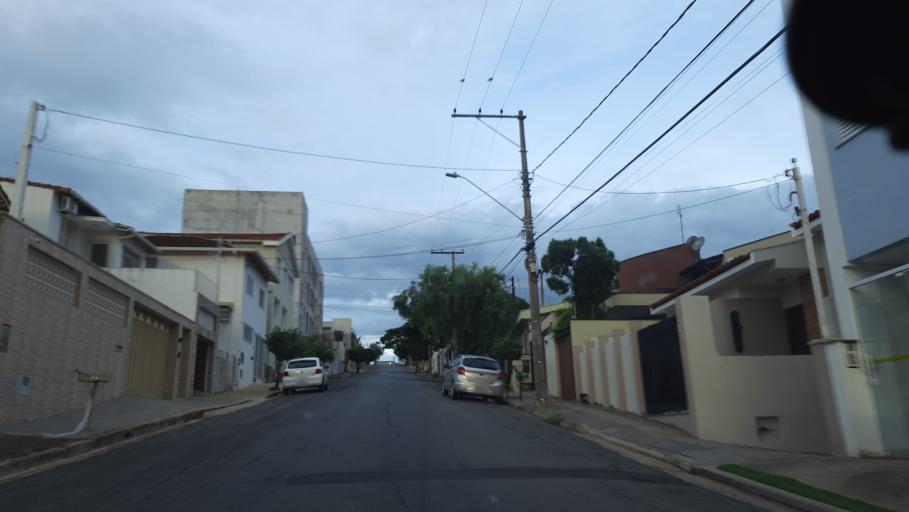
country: BR
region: Sao Paulo
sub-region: Sao Joao Da Boa Vista
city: Sao Joao da Boa Vista
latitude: -21.9668
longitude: -46.7933
